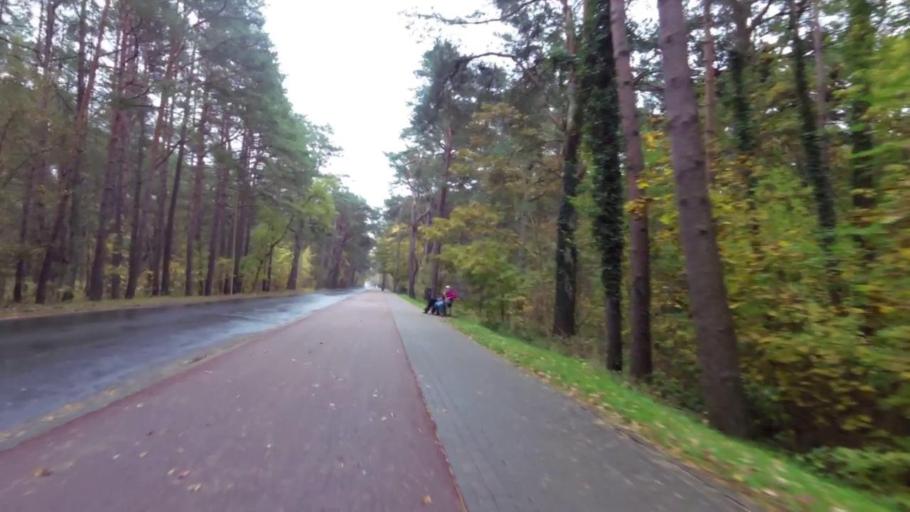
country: PL
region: West Pomeranian Voivodeship
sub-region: Swinoujscie
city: Swinoujscie
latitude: 53.9244
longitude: 14.2323
